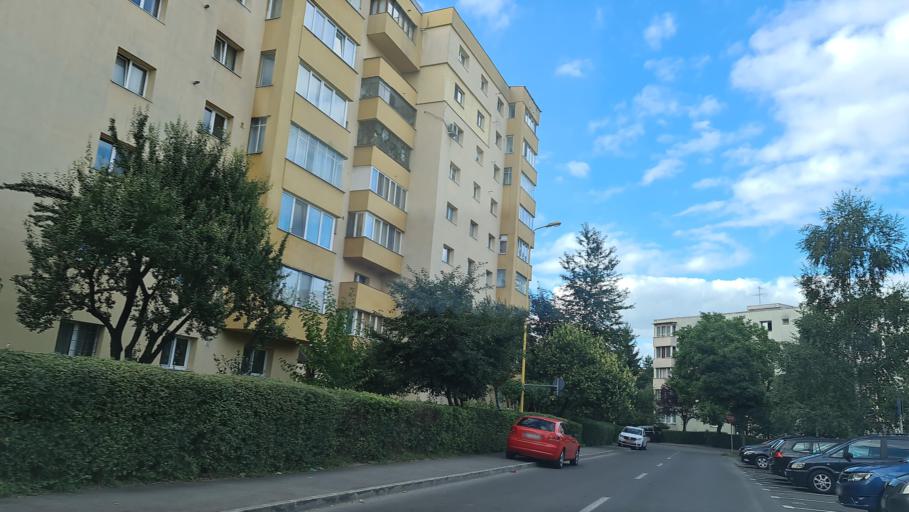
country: RO
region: Brasov
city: Brasov
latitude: 45.6449
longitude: 25.6190
